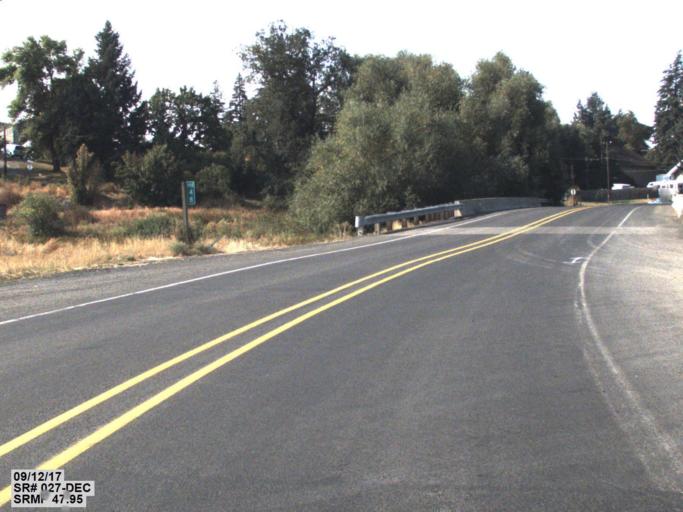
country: US
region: Idaho
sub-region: Benewah County
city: Plummer
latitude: 47.2204
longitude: -117.0743
